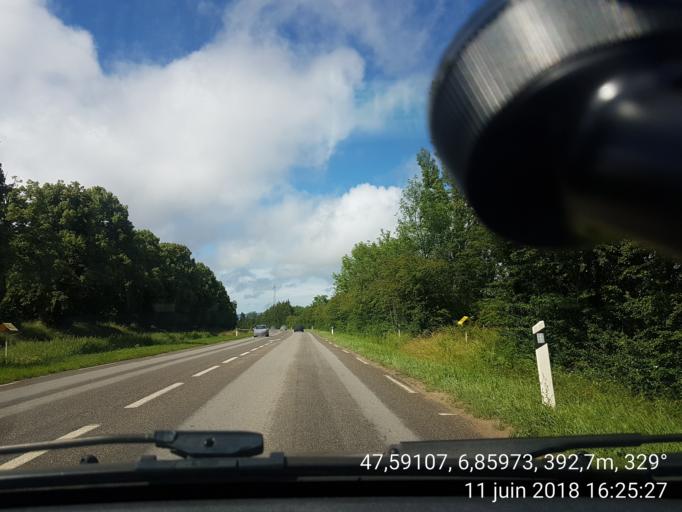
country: FR
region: Franche-Comte
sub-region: Territoire de Belfort
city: Andelnans
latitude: 47.5913
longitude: 6.8600
